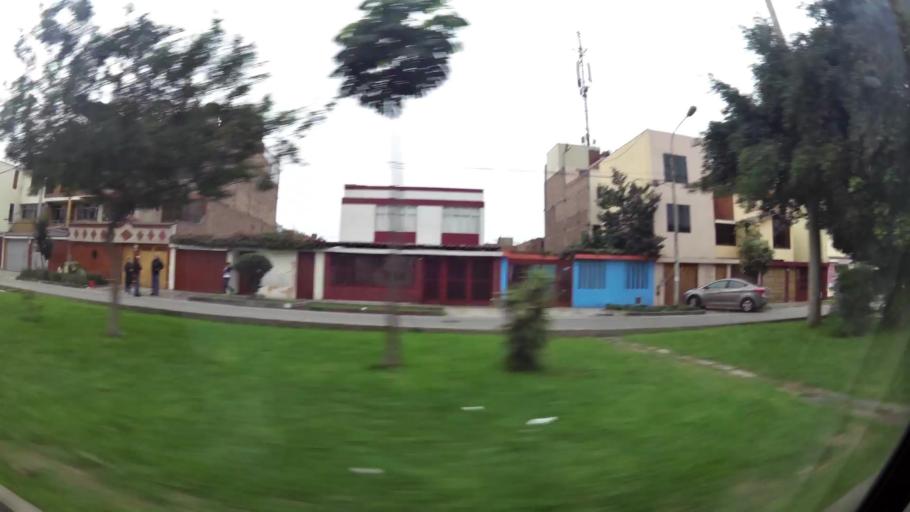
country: PE
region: Lima
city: Lima
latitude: -12.0658
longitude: -77.0674
